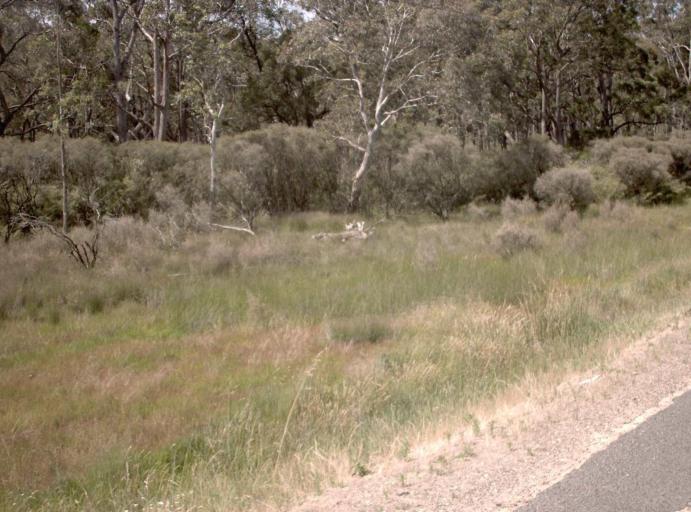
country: AU
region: Victoria
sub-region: Wellington
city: Sale
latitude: -37.9144
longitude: 147.3007
